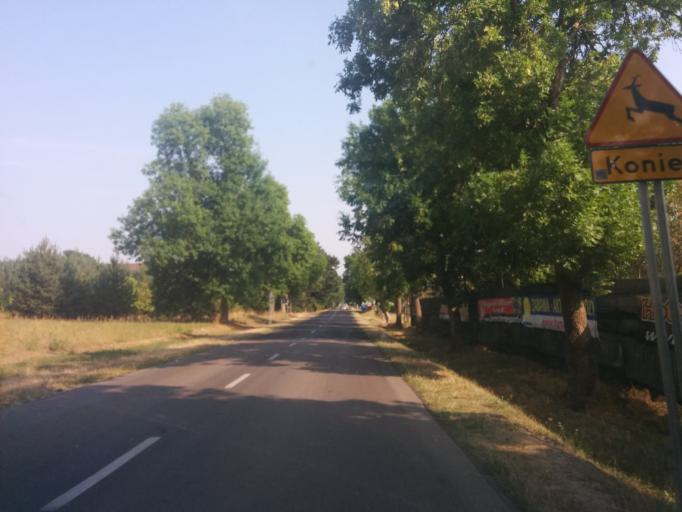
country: PL
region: Silesian Voivodeship
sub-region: Powiat zawiercianski
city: Kroczyce
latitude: 50.5690
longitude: 19.5281
